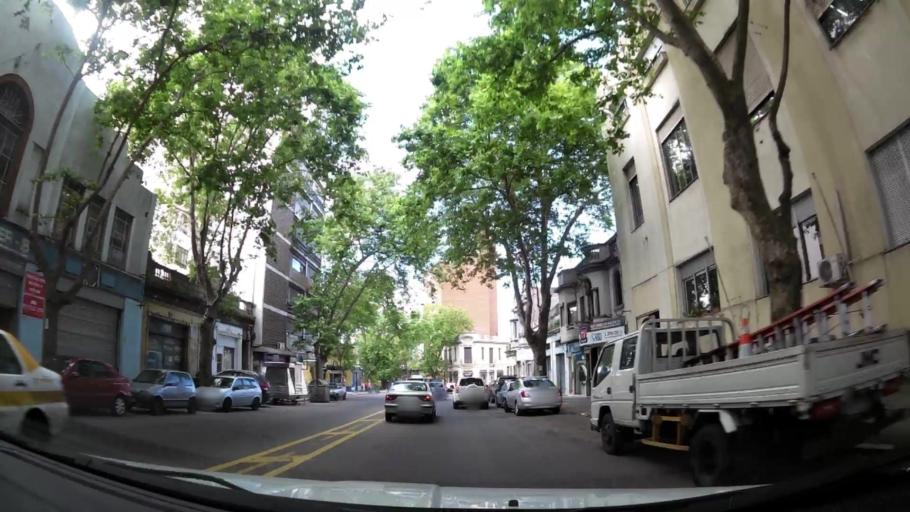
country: UY
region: Montevideo
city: Montevideo
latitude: -34.8769
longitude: -56.1859
